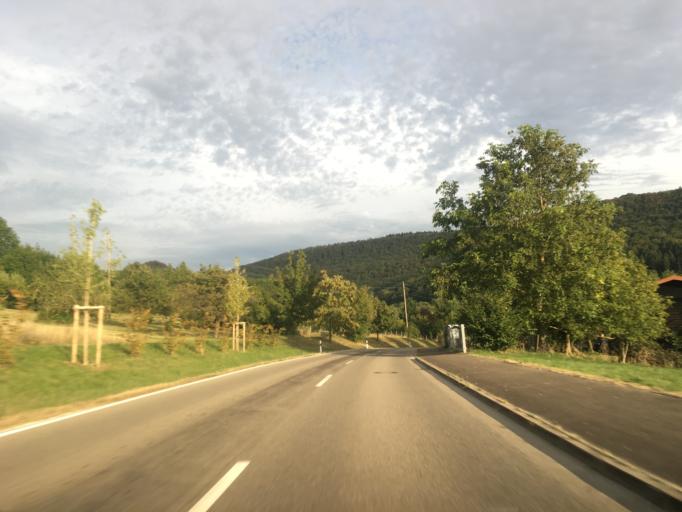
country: DE
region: Baden-Wuerttemberg
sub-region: Tuebingen Region
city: Eningen unter Achalm
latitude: 48.4930
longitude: 9.2692
